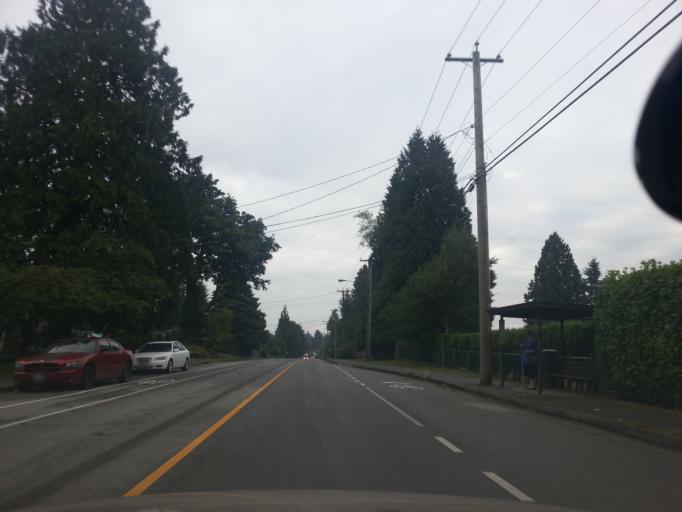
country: CA
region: British Columbia
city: Port Moody
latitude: 49.2745
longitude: -122.8807
